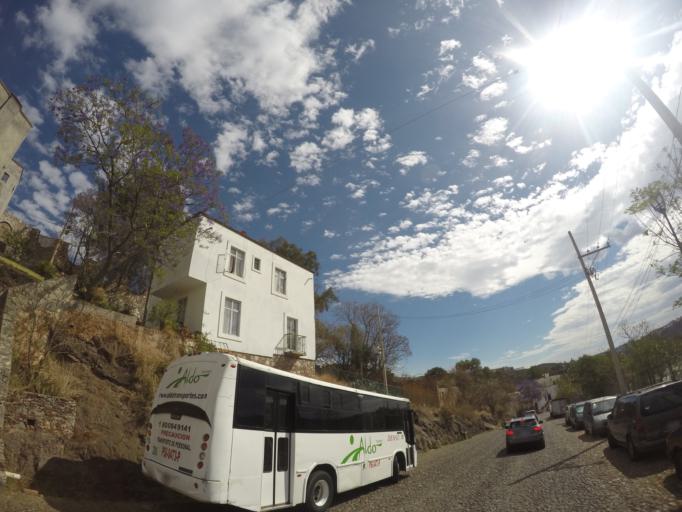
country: MX
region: Guanajuato
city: Guanajuato
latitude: 21.0137
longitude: -101.2641
